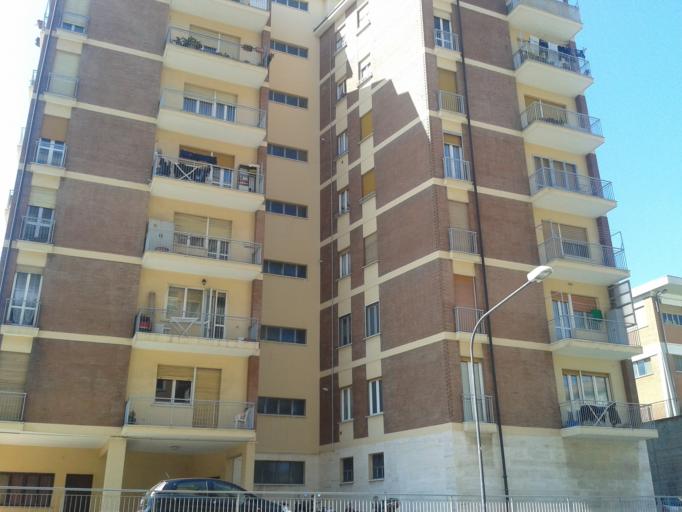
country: IT
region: Liguria
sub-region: Provincia di Savona
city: Savona
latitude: 44.3041
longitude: 8.4706
